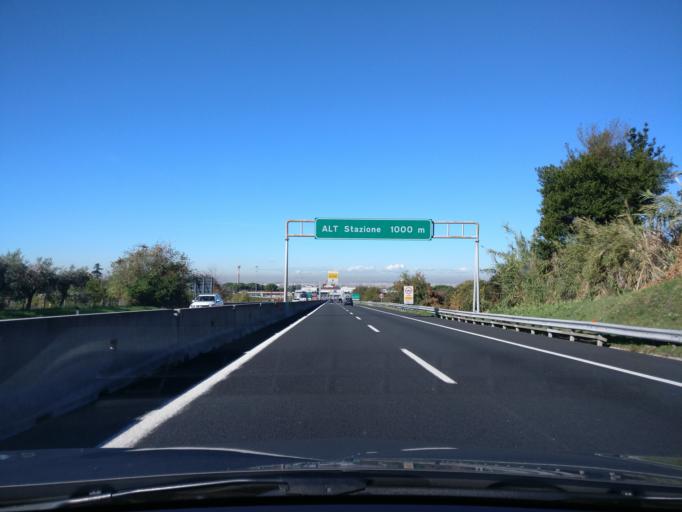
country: IT
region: Latium
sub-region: Citta metropolitana di Roma Capitale
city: Frascati
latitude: 41.8294
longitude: 12.6632
